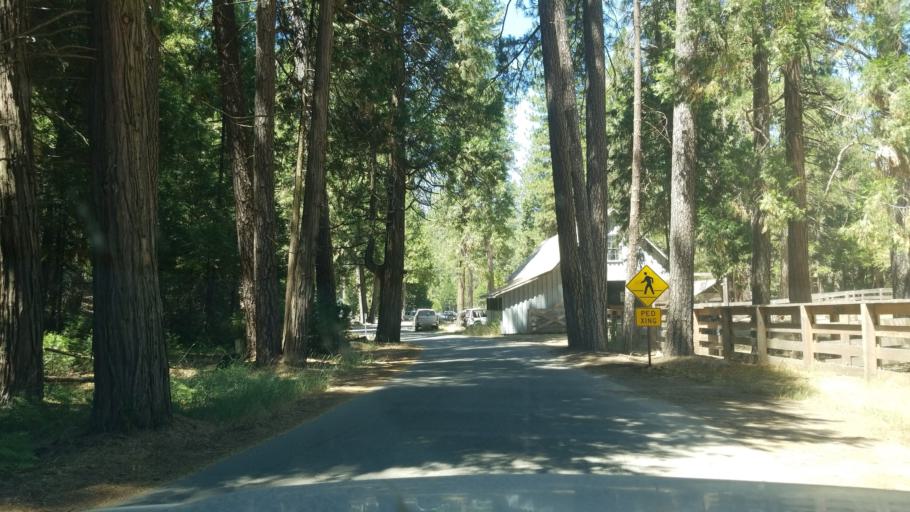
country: US
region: California
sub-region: Madera County
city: Ahwahnee
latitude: 37.5381
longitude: -119.6552
